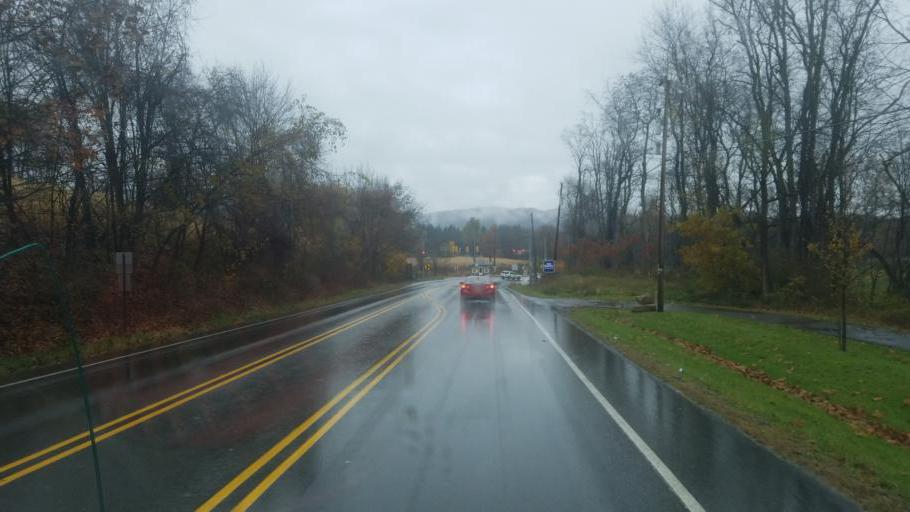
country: US
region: Pennsylvania
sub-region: Clinton County
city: Mill Hall
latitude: 41.1104
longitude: -77.5048
